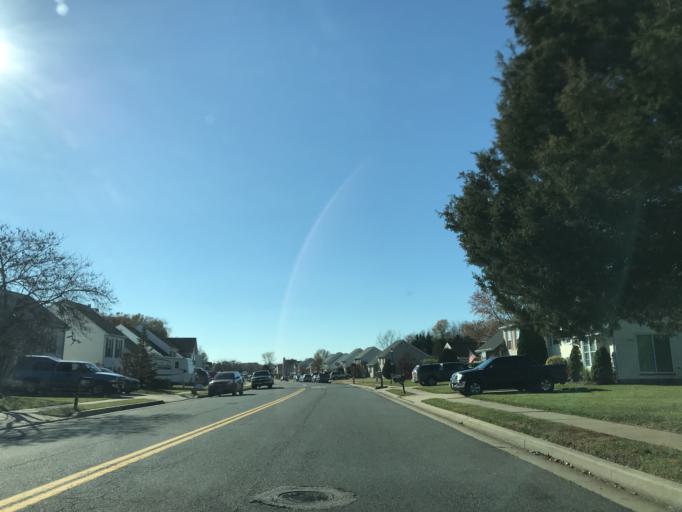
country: US
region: Maryland
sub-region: Baltimore County
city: Bowleys Quarters
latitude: 39.3680
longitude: -76.3548
